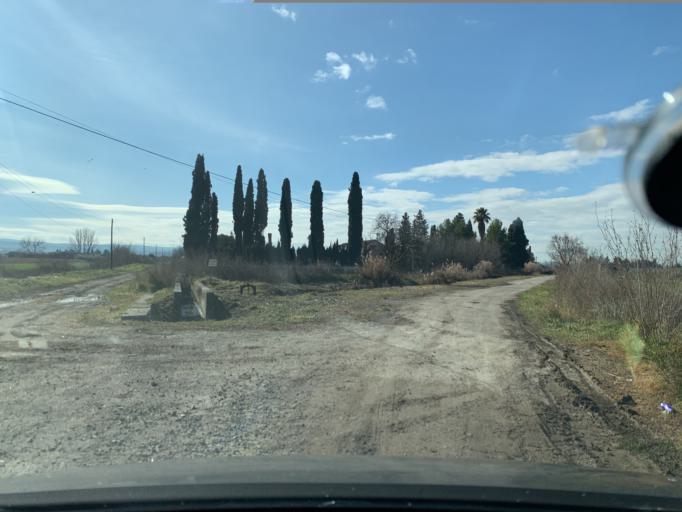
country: ES
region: Andalusia
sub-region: Provincia de Granada
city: Chauchina
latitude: 37.1869
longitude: -3.7586
